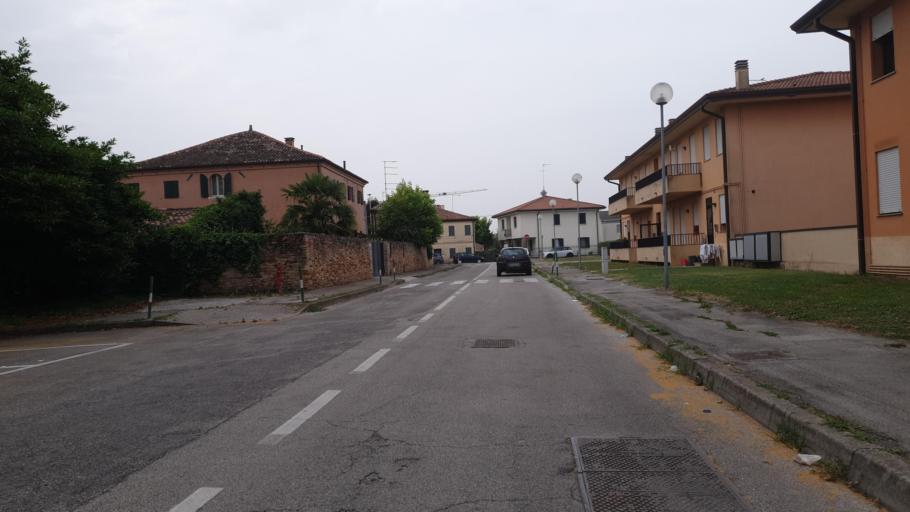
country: IT
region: Veneto
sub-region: Provincia di Padova
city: Piove di Sacco-Piovega
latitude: 45.2876
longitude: 12.0291
